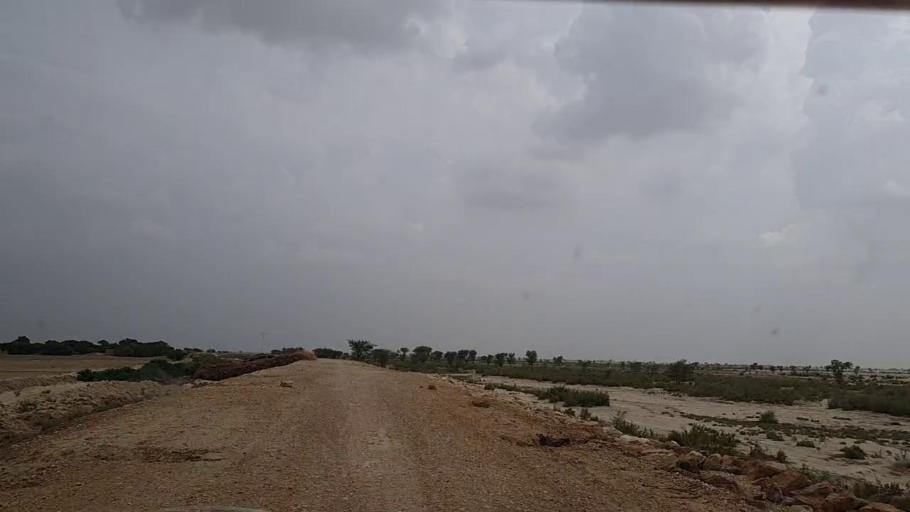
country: PK
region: Sindh
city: Johi
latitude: 26.7257
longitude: 67.5780
